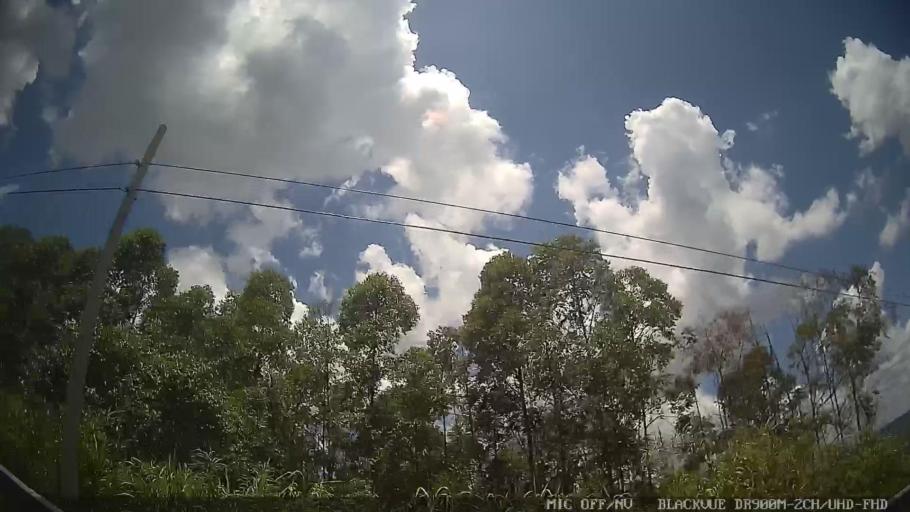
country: BR
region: Sao Paulo
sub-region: Amparo
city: Amparo
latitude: -22.6530
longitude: -46.7432
